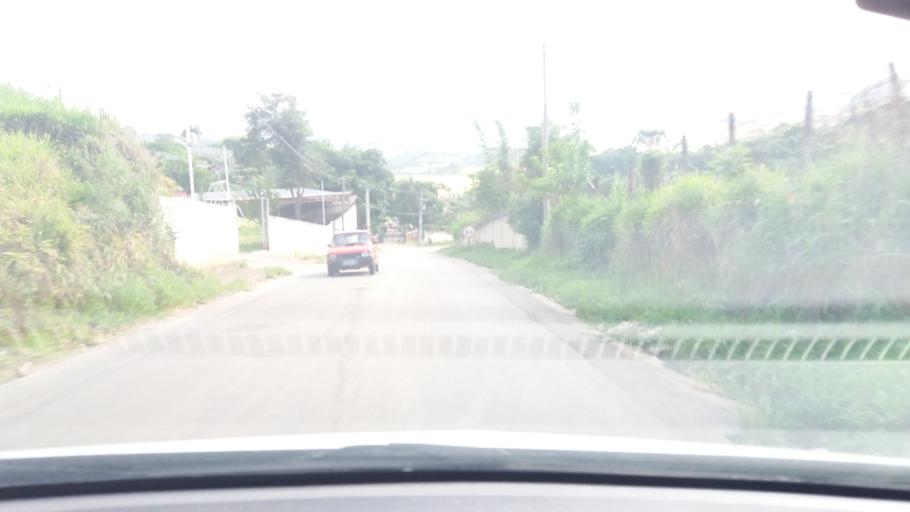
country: BR
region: Sao Paulo
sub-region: Bom Jesus Dos Perdoes
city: Bom Jesus dos Perdoes
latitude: -23.1489
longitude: -46.4697
